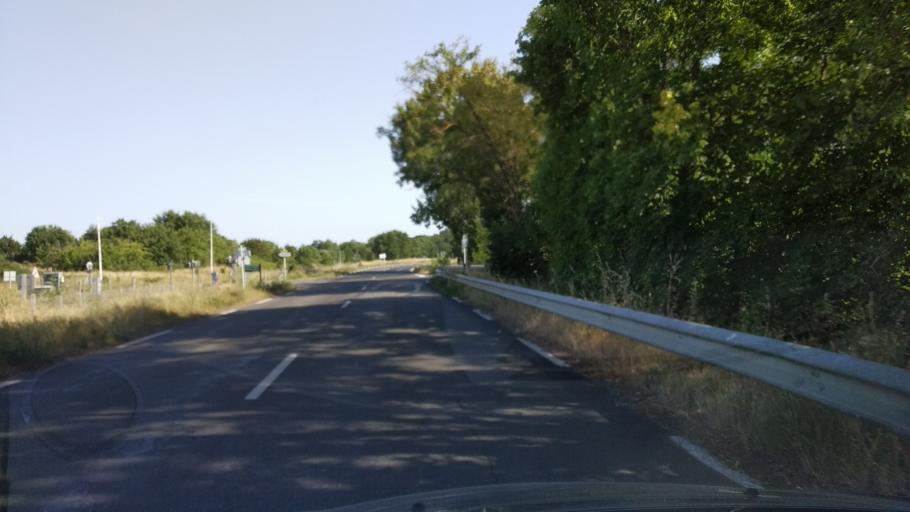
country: FR
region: Poitou-Charentes
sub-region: Departement de la Vienne
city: Lussac-les-Chateaux
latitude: 46.4446
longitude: 0.6559
